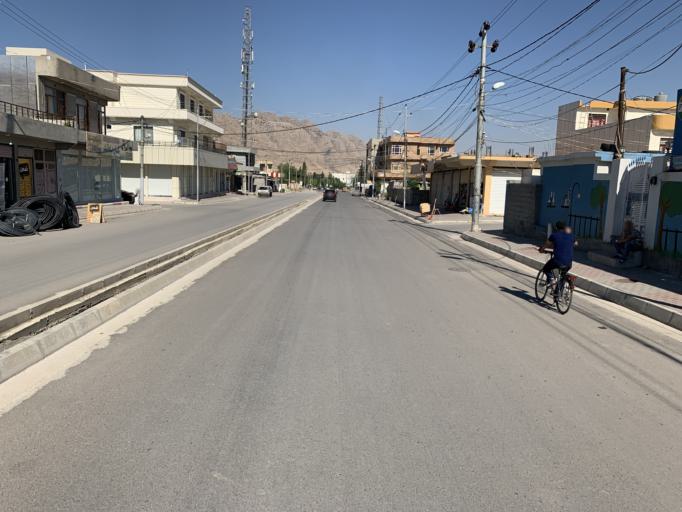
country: IQ
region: As Sulaymaniyah
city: Raniye
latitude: 36.2571
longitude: 44.8750
